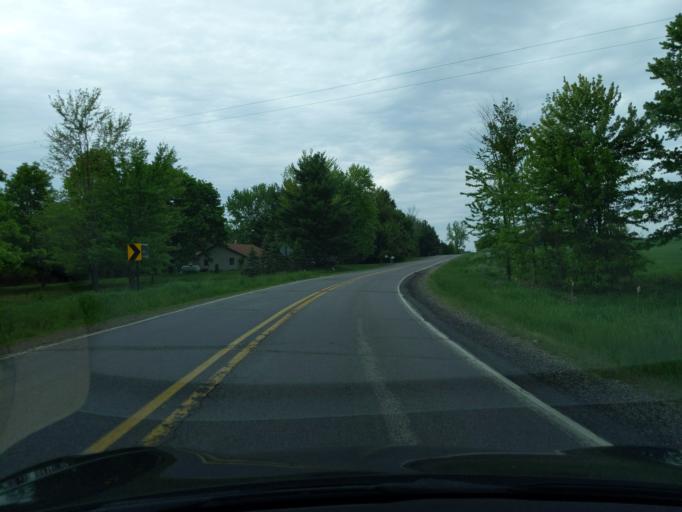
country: US
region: Michigan
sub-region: Ingham County
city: Mason
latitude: 42.6191
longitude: -84.3638
